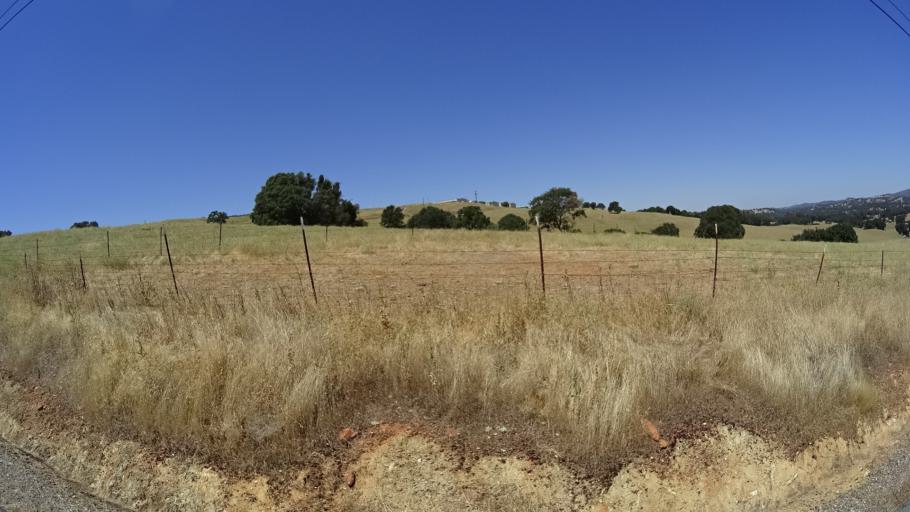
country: US
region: California
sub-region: Calaveras County
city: San Andreas
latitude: 38.1434
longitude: -120.6405
